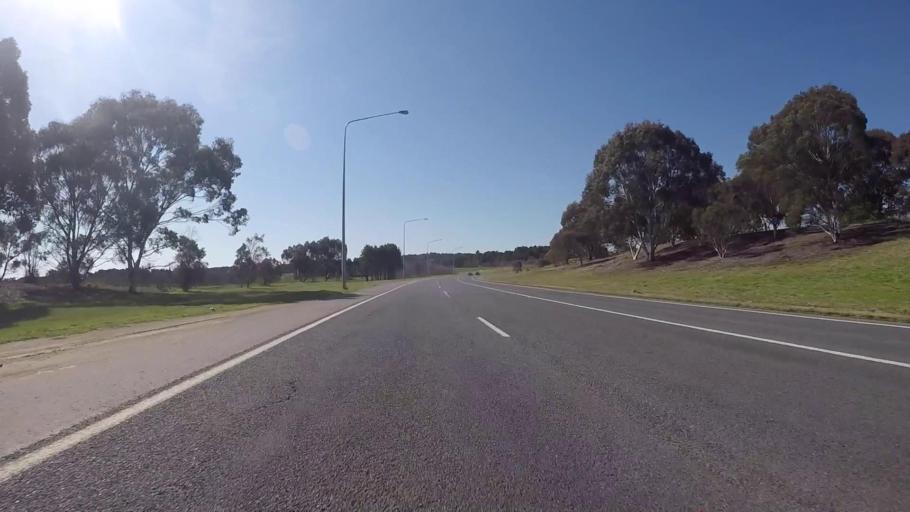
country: AU
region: Australian Capital Territory
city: Forrest
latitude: -35.3181
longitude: 149.0894
